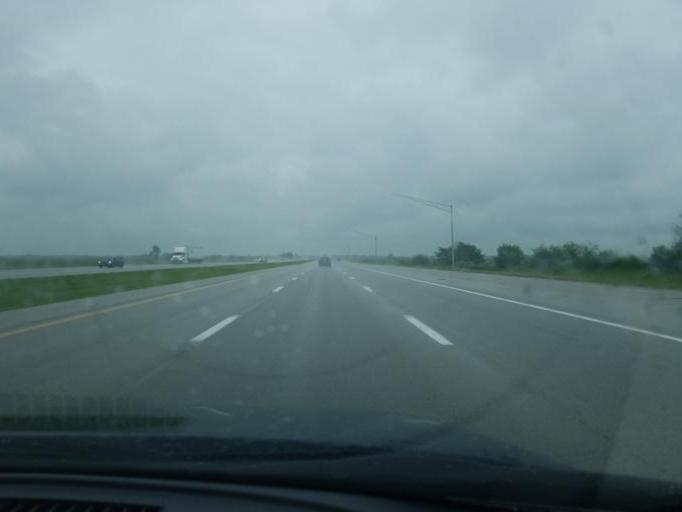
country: US
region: Ohio
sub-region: Fayette County
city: Jeffersonville
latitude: 39.6352
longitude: -83.5763
